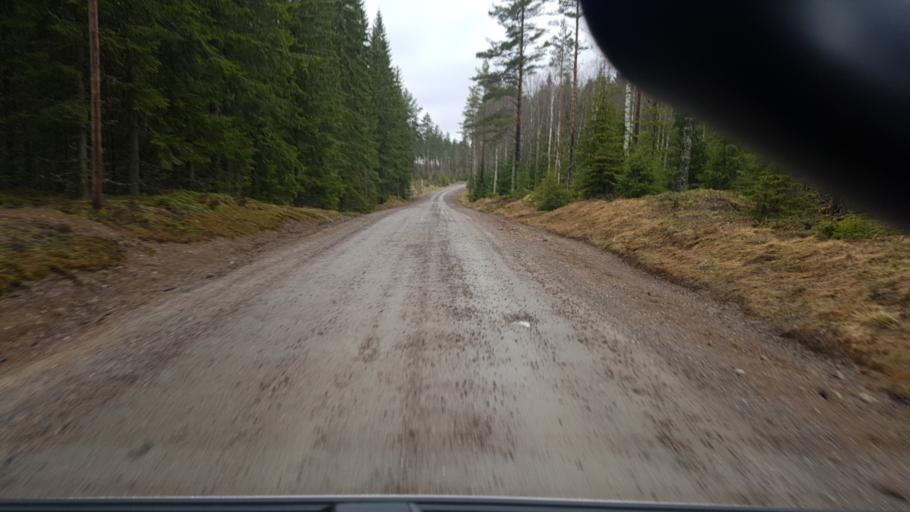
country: SE
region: Vaermland
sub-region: Eda Kommun
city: Charlottenberg
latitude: 59.9770
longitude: 12.4919
